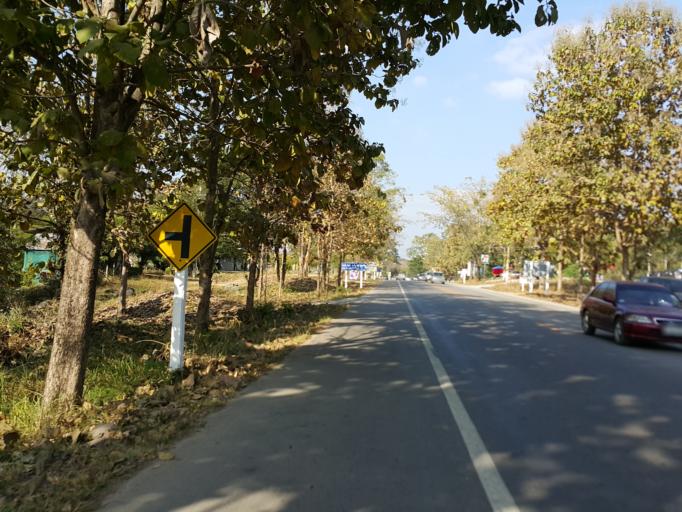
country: TH
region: Chiang Mai
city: Mae On
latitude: 18.7946
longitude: 99.2442
